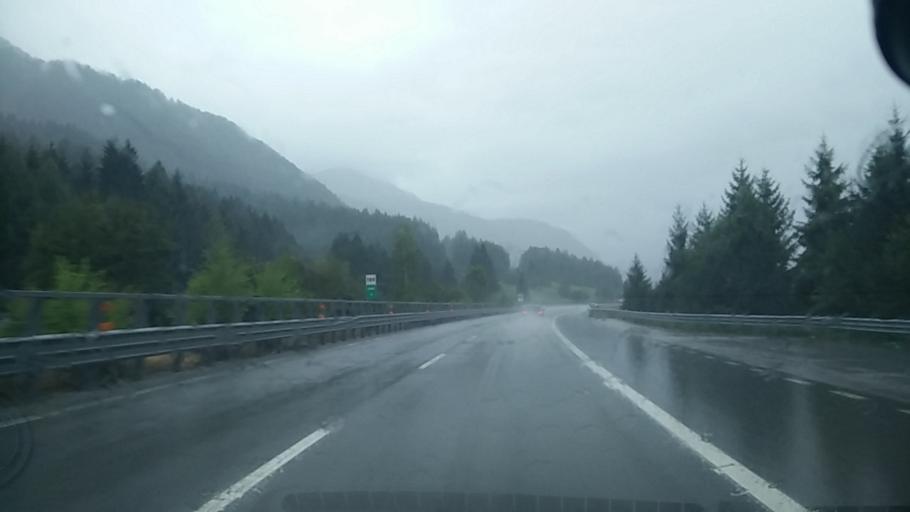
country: IT
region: Friuli Venezia Giulia
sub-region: Provincia di Udine
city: Malborghetto
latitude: 46.4977
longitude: 13.4174
